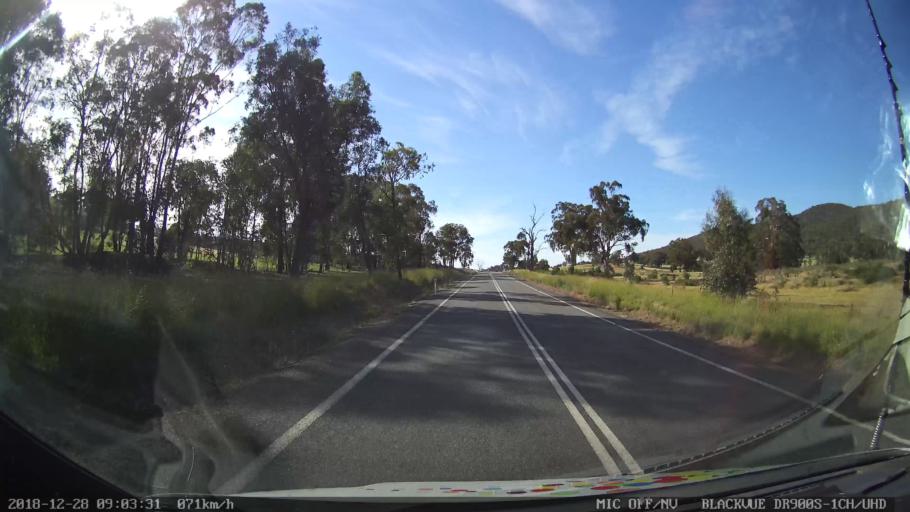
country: AU
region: New South Wales
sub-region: Upper Lachlan Shire
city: Crookwell
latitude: -34.1642
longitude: 149.3378
